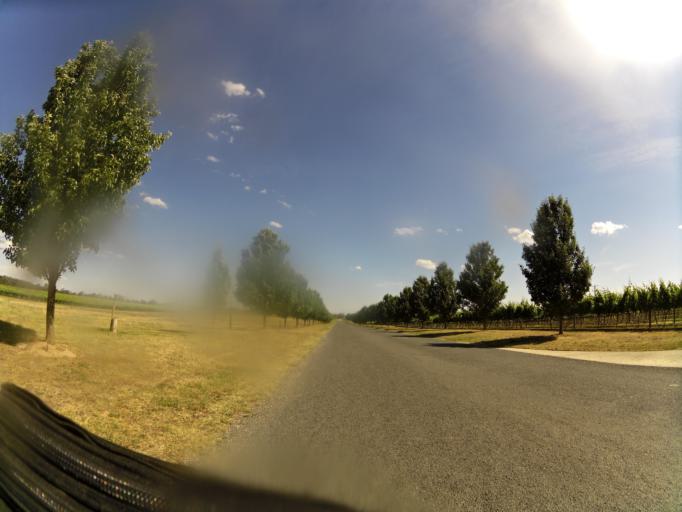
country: AU
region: Victoria
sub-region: Campaspe
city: Kyabram
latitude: -36.8503
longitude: 145.0901
